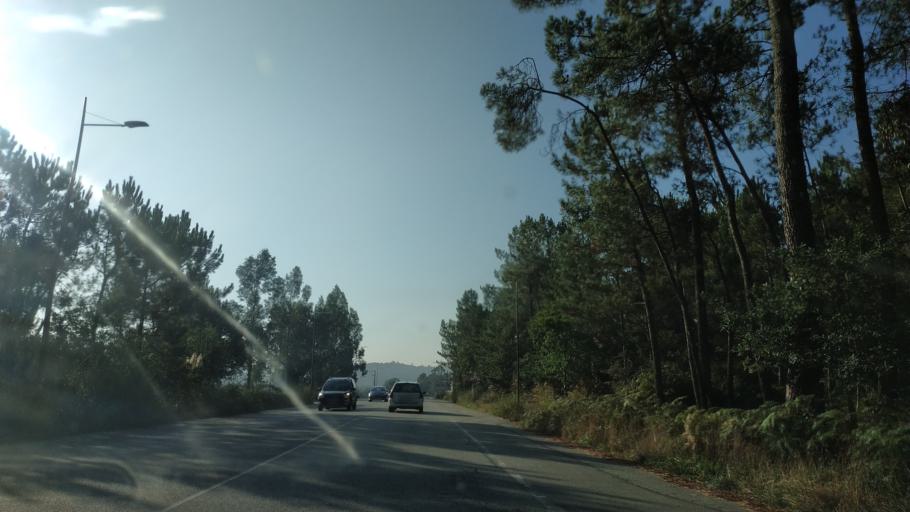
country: ES
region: Galicia
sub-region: Provincia da Coruna
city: Carballo
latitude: 43.2303
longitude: -8.6776
